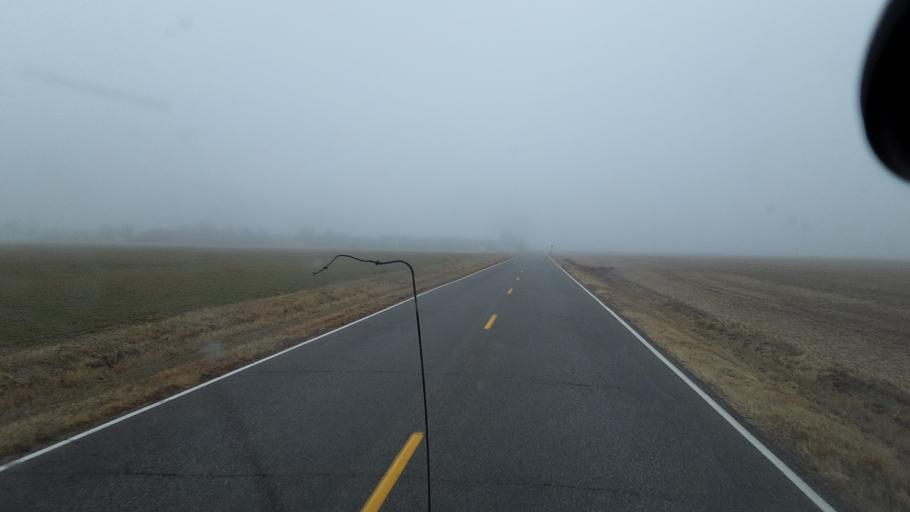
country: US
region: Kansas
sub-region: Reno County
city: South Hutchinson
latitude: 37.9657
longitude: -98.0138
